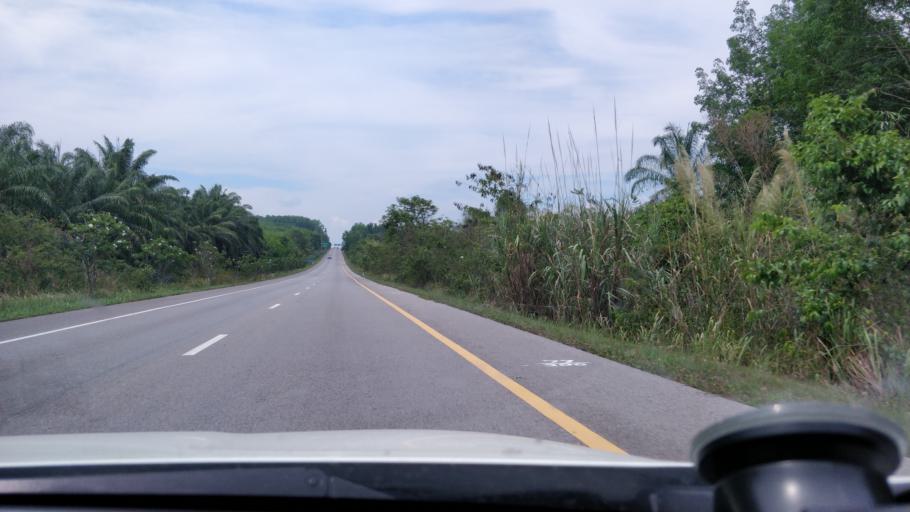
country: TH
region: Surat Thani
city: Khian Sa
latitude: 8.8059
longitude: 99.1640
